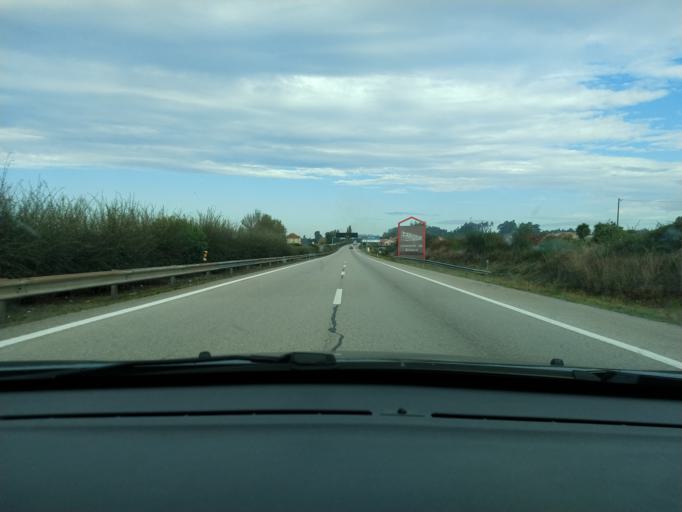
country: PT
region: Aveiro
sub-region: Estarreja
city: Beduido
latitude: 40.7627
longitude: -8.5405
